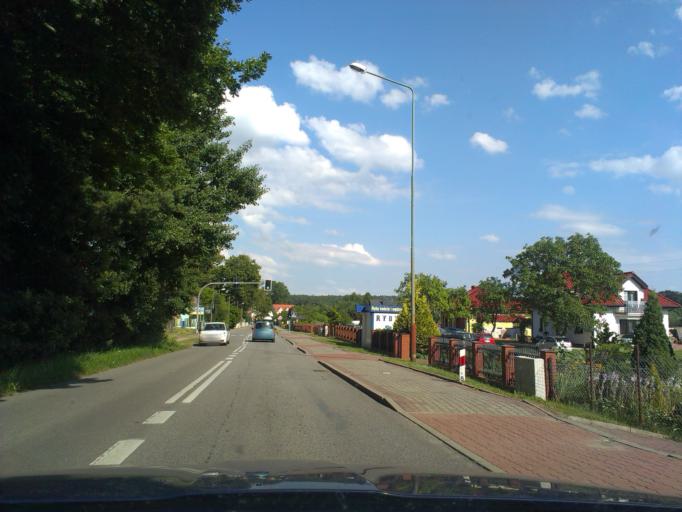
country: PL
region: West Pomeranian Voivodeship
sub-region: Powiat kamienski
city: Miedzyzdroje
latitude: 53.9657
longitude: 14.5634
